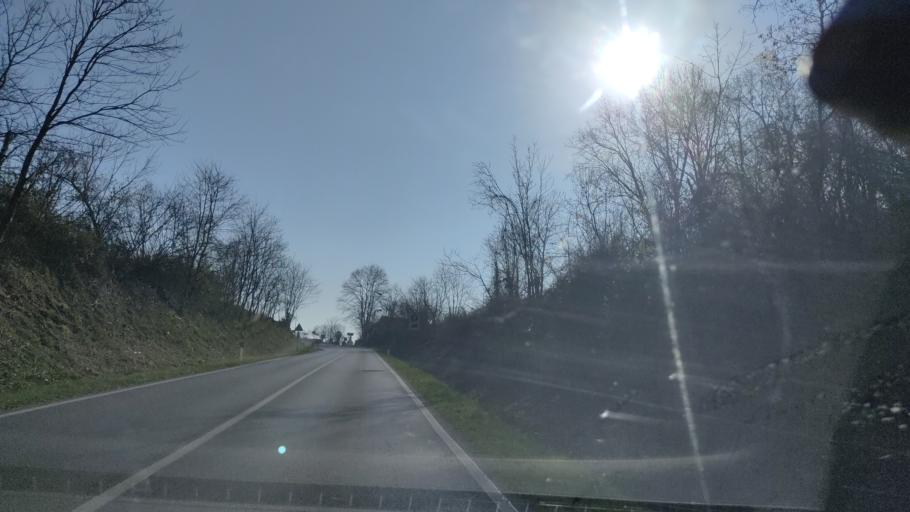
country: IT
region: Friuli Venezia Giulia
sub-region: Provincia di Pordenone
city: Budoia
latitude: 46.0426
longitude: 12.5218
